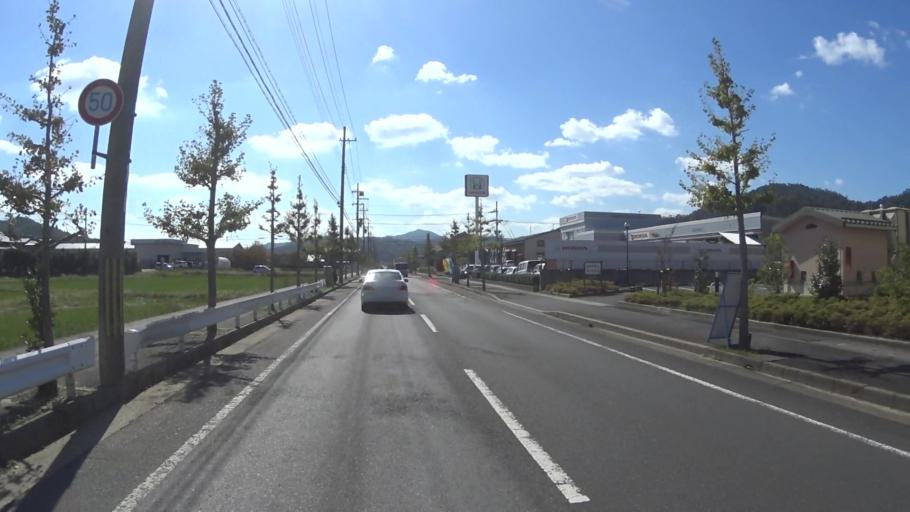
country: JP
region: Kyoto
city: Miyazu
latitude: 35.6779
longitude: 135.0248
